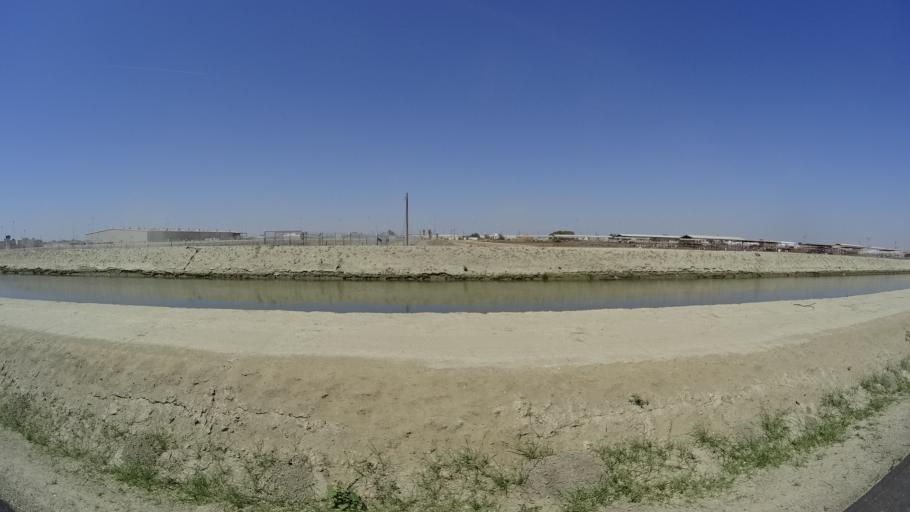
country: US
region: California
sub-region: Kings County
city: Corcoran
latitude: 36.0589
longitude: -119.5363
